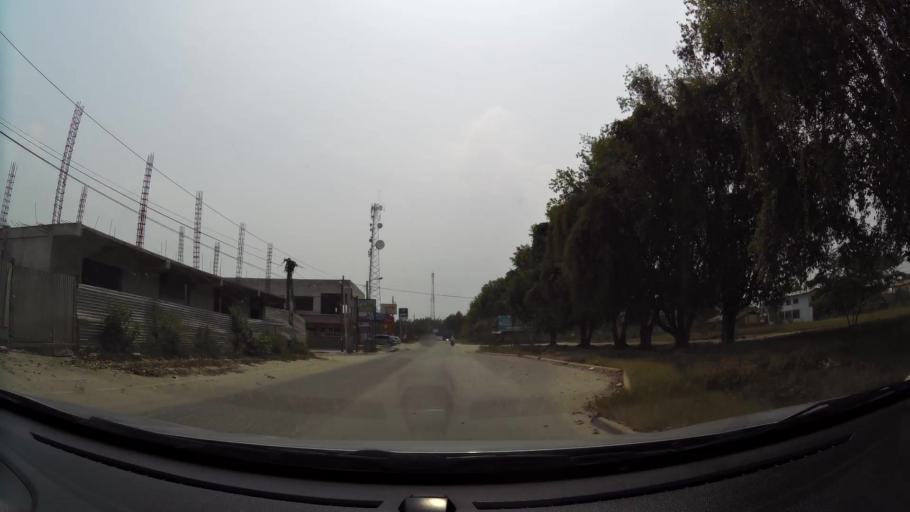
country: HN
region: Cortes
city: La Lima
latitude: 15.4364
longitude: -87.9118
